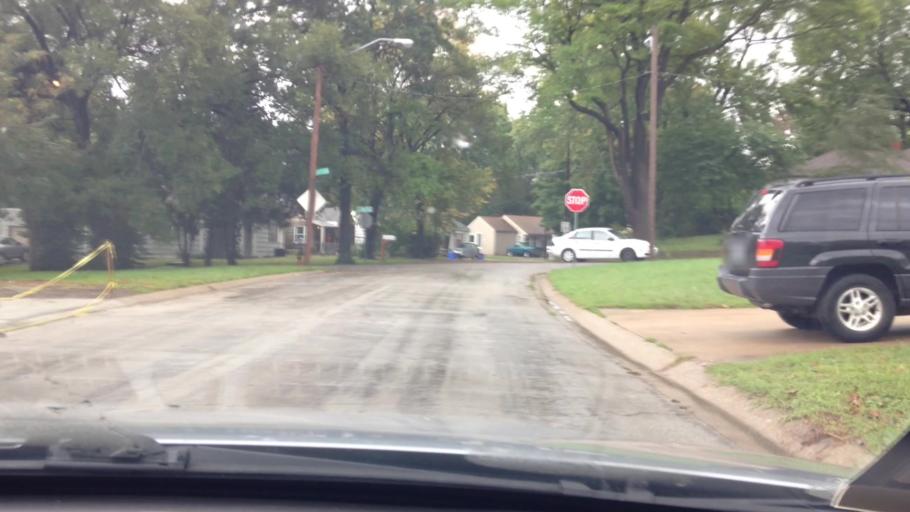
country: US
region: Missouri
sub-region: Clay County
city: Gladstone
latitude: 39.1779
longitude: -94.5730
